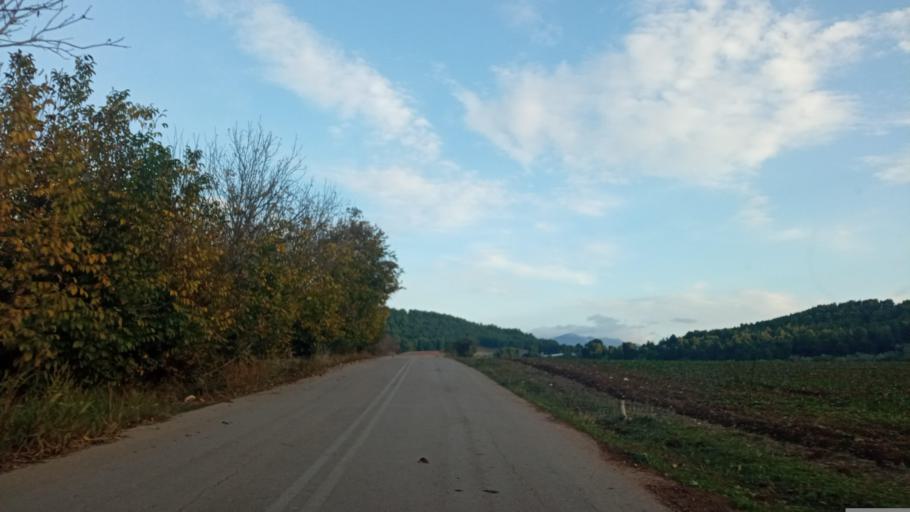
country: GR
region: Central Greece
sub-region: Nomos Evvoias
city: Kastella
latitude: 38.5512
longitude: 23.7155
